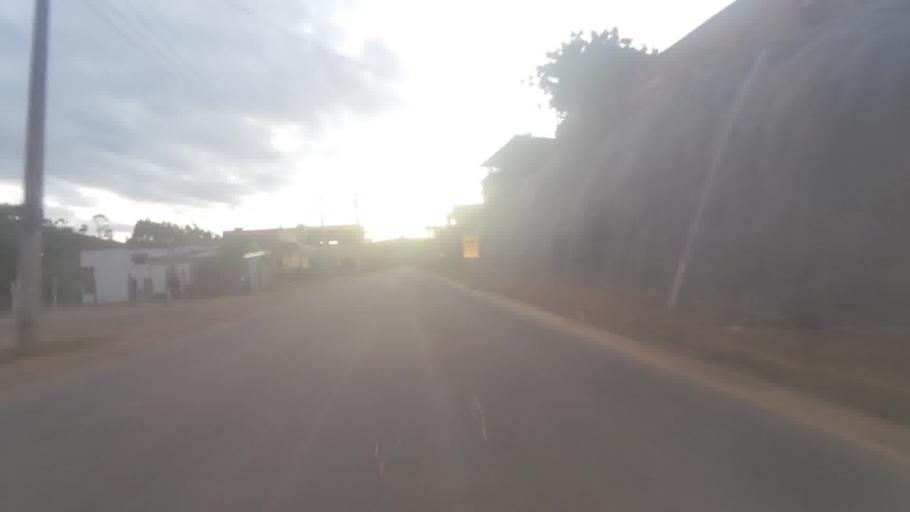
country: BR
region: Espirito Santo
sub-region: Itapemirim
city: Itapemirim
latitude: -20.9391
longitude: -40.8850
